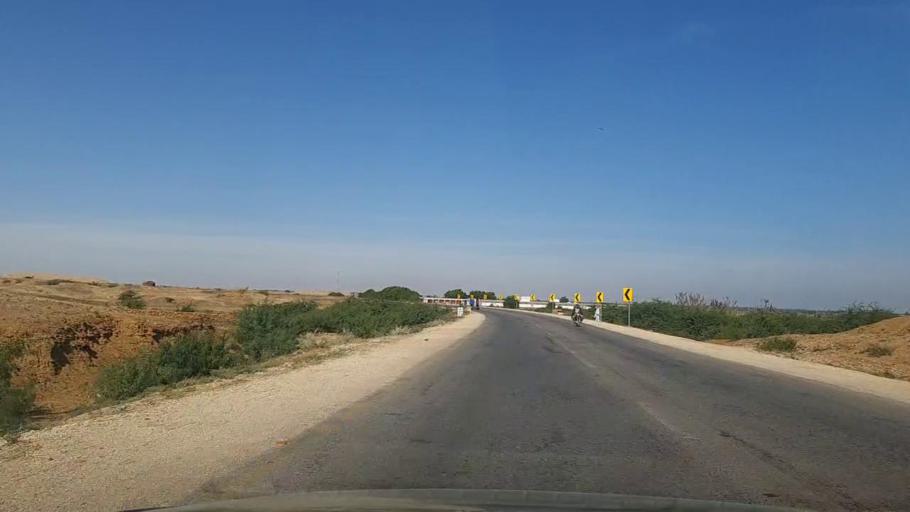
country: PK
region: Sindh
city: Kotri
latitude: 25.1867
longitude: 68.2401
